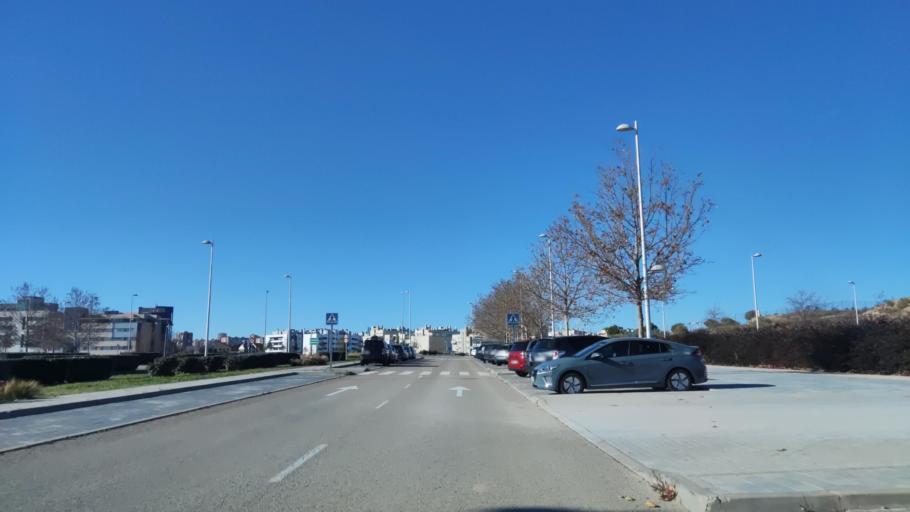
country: ES
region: Madrid
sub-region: Provincia de Madrid
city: Hortaleza
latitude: 40.4826
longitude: -3.6234
